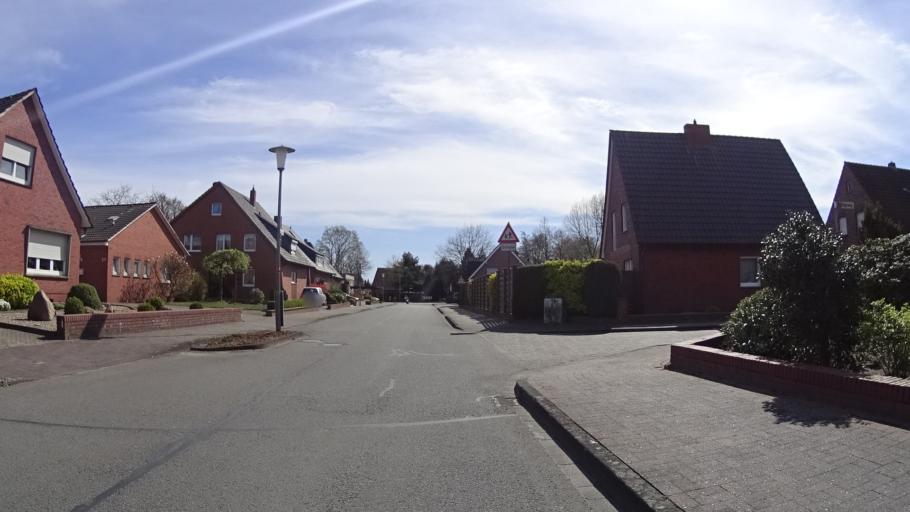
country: DE
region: North Rhine-Westphalia
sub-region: Regierungsbezirk Munster
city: Dreierwalde
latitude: 52.2785
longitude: 7.4776
